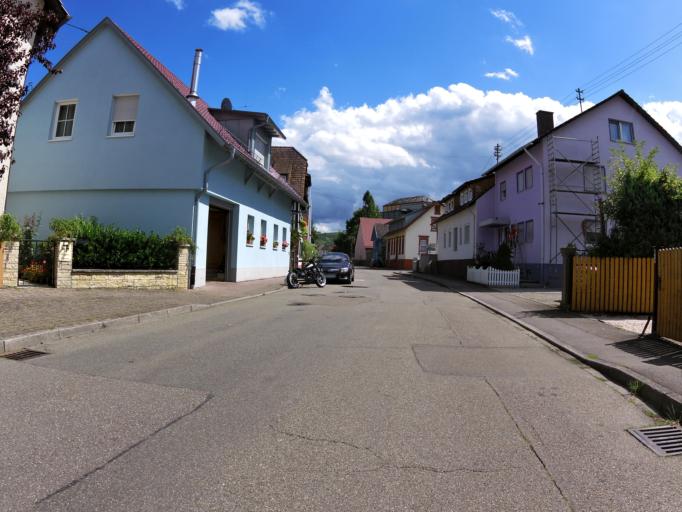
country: DE
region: Baden-Wuerttemberg
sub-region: Freiburg Region
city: Lahr
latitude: 48.3614
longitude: 7.8344
